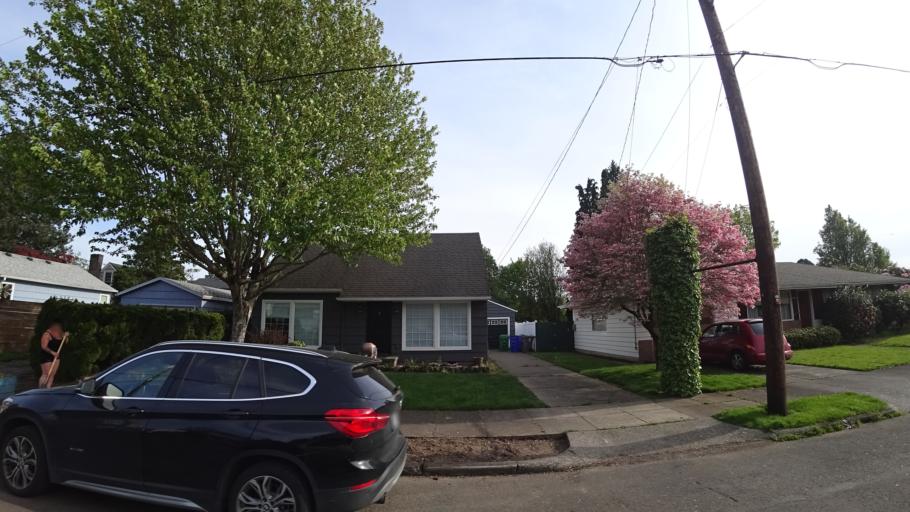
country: US
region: Oregon
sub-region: Clackamas County
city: Milwaukie
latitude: 45.4664
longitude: -122.6164
